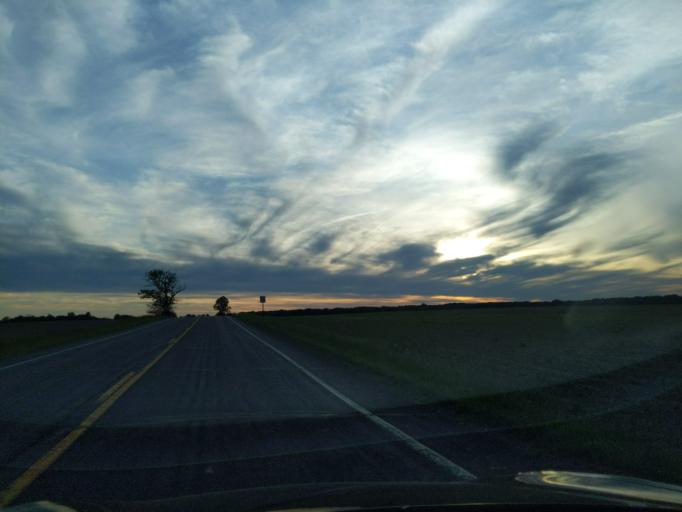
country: US
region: Michigan
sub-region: Ingham County
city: Williamston
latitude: 42.6010
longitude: -84.3093
